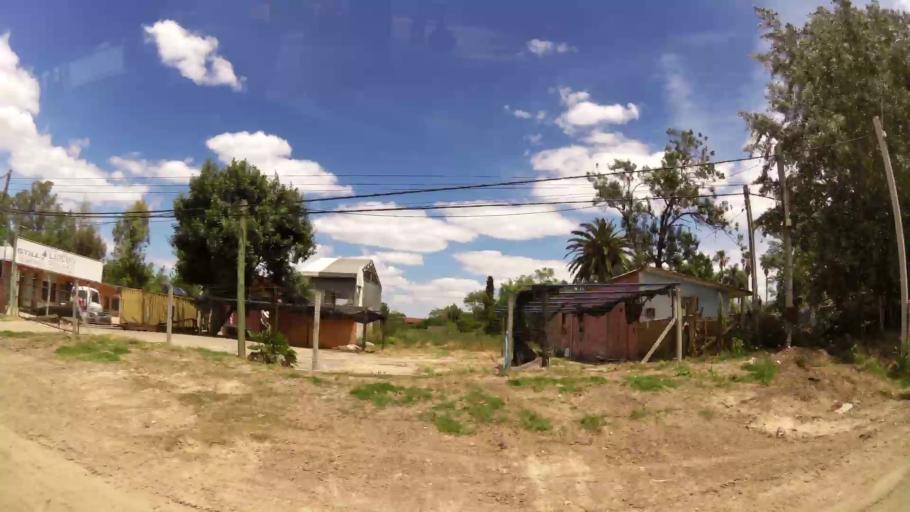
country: UY
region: Canelones
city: Colonia Nicolich
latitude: -34.8165
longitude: -55.9711
